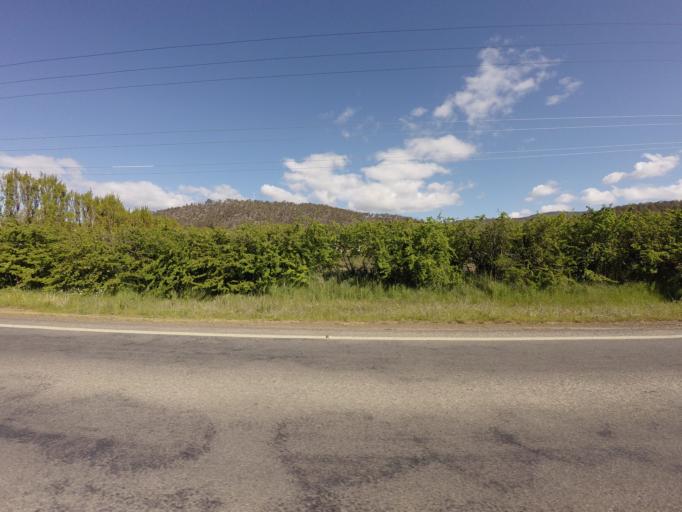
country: AU
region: Tasmania
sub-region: Derwent Valley
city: New Norfolk
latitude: -42.7781
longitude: 147.0474
